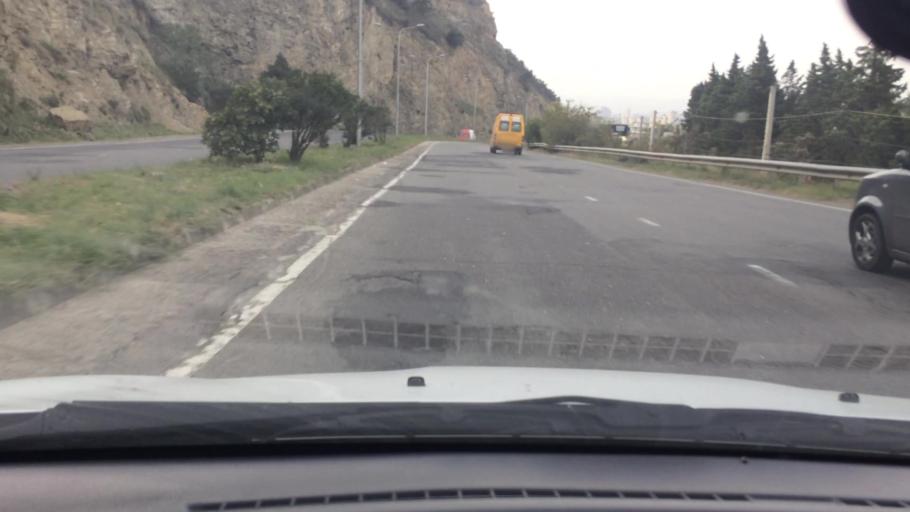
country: GE
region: T'bilisi
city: Tbilisi
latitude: 41.6579
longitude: 44.8922
